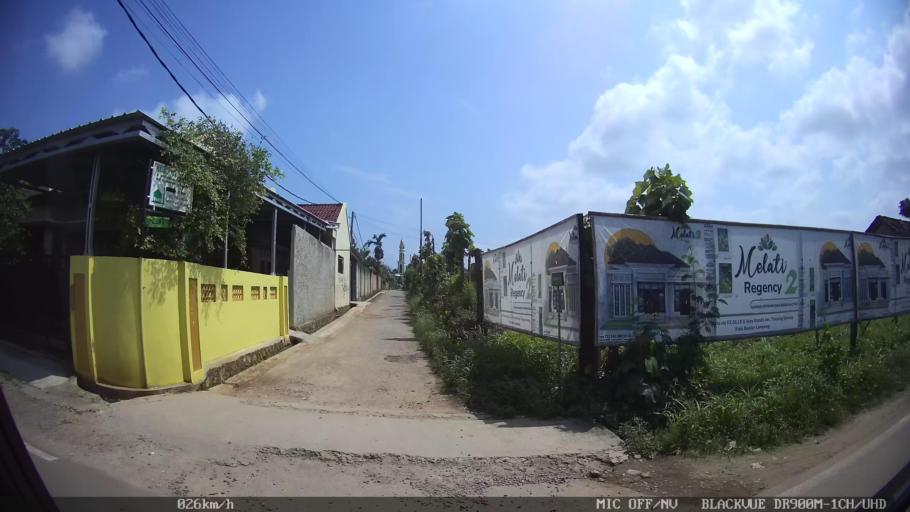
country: ID
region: Lampung
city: Kedaton
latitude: -5.3491
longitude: 105.2816
